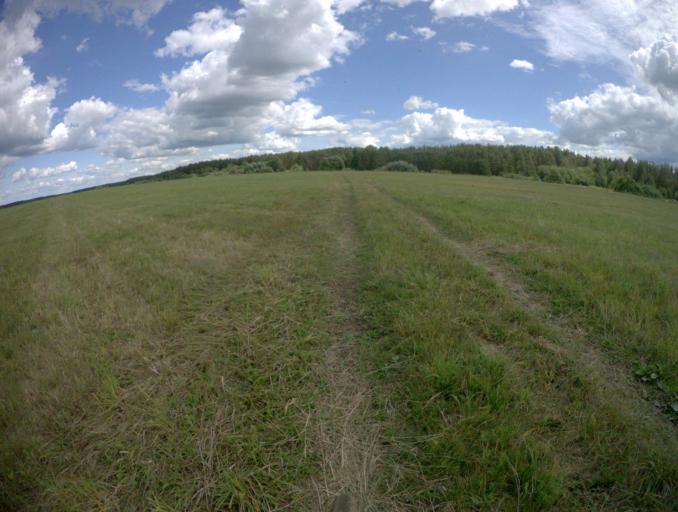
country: RU
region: Vladimir
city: Orgtrud
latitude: 56.3010
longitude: 40.6819
